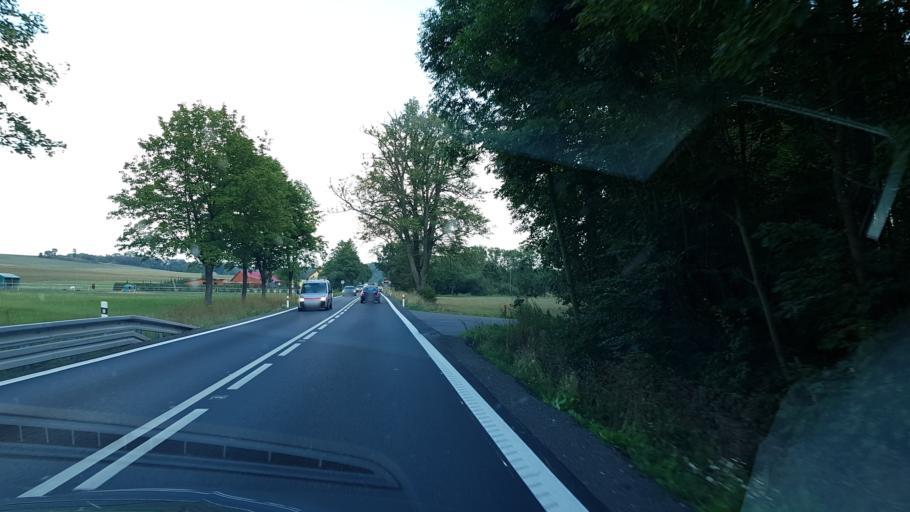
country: CZ
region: Pardubicky
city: Zamberk
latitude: 50.0958
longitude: 16.4192
